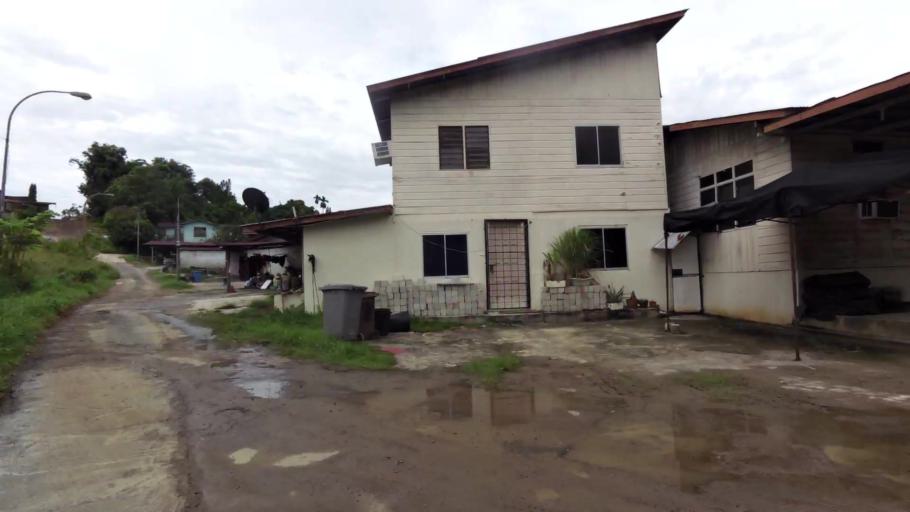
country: BN
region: Brunei and Muara
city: Bandar Seri Begawan
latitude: 4.8968
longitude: 114.9316
